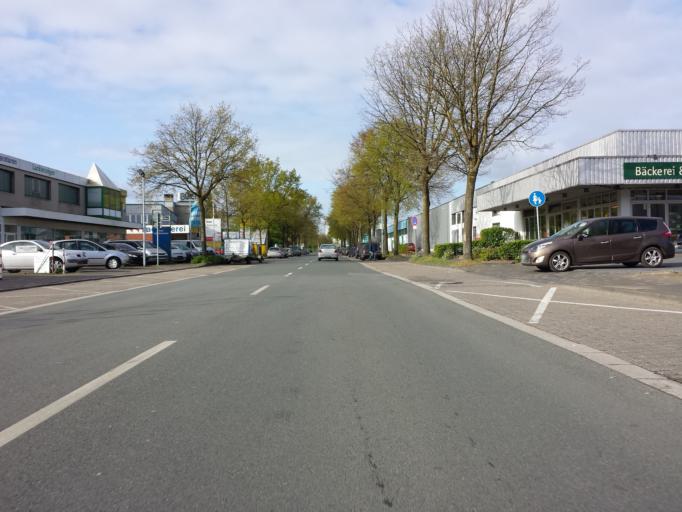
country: DE
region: North Rhine-Westphalia
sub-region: Regierungsbezirk Detmold
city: Guetersloh
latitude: 51.8880
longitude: 8.3583
